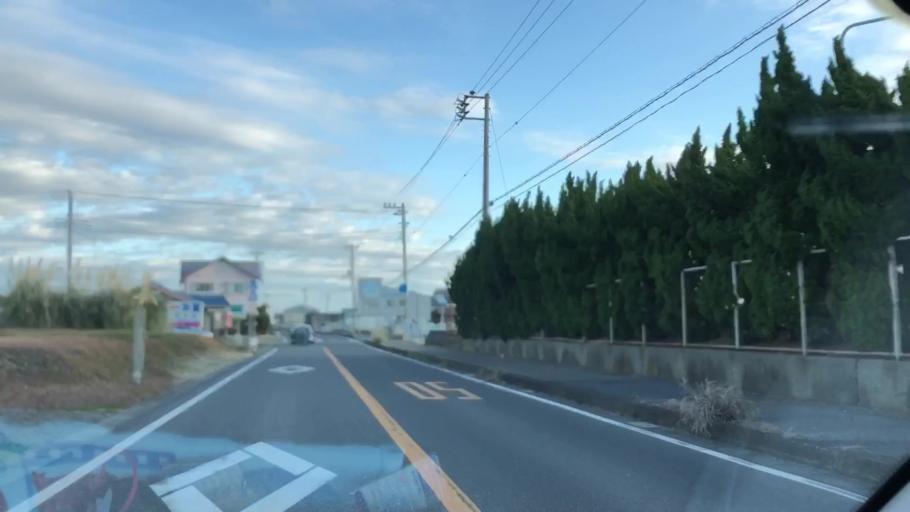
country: JP
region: Chiba
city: Tateyama
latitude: 34.9387
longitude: 139.9594
